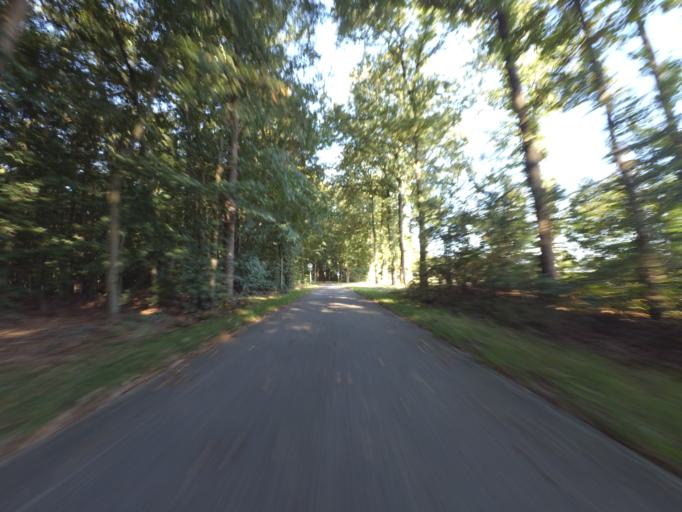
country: NL
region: Gelderland
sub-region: Gemeente Barneveld
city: Garderen
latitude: 52.2617
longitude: 5.7075
